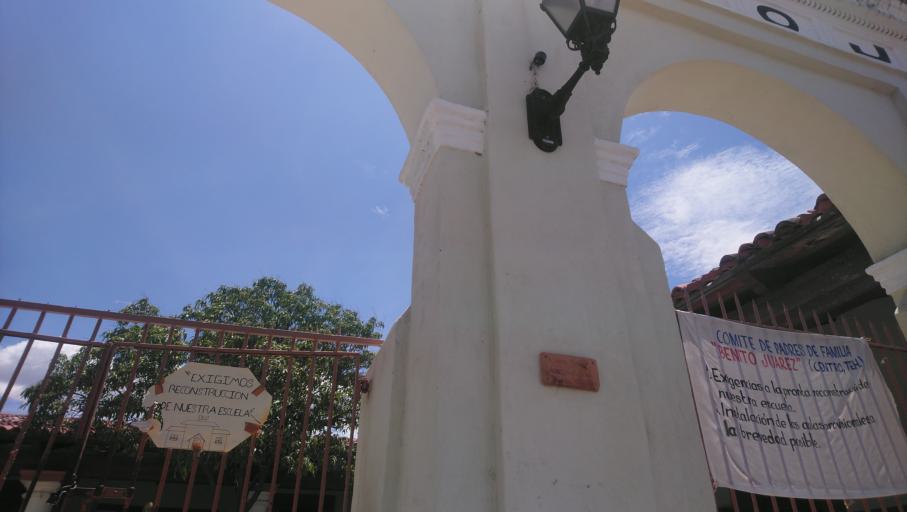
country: MX
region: Oaxaca
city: San Blas Atempa
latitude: 16.3335
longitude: -95.2322
